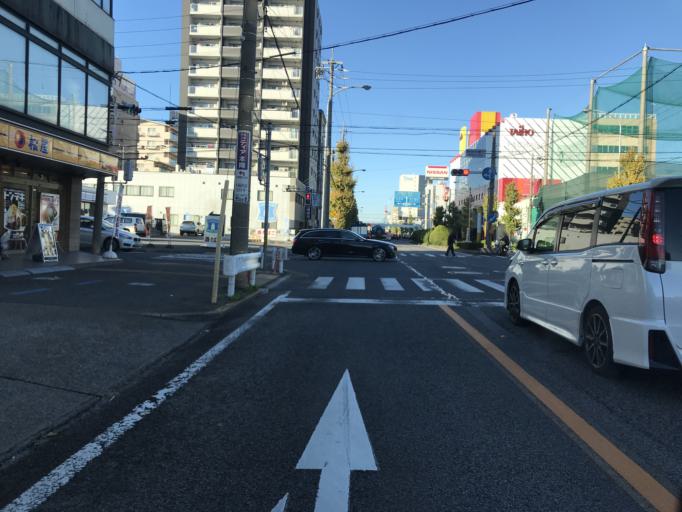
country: JP
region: Aichi
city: Nagoya-shi
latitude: 35.1759
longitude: 136.8728
